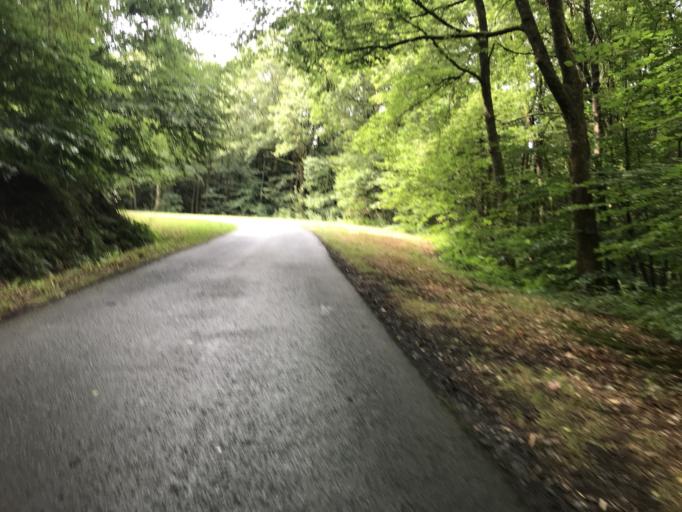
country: FR
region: Champagne-Ardenne
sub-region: Departement des Ardennes
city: Thilay
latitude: 49.8926
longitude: 4.7709
